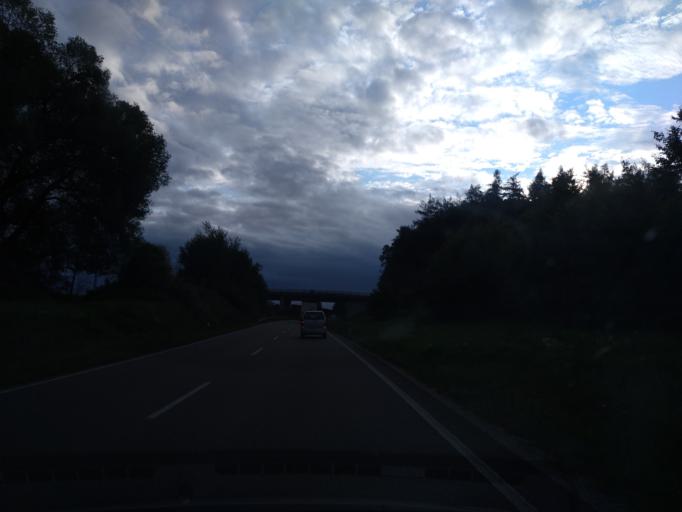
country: DE
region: Bavaria
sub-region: Upper Bavaria
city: Oberhausen
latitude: 48.7160
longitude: 11.0852
